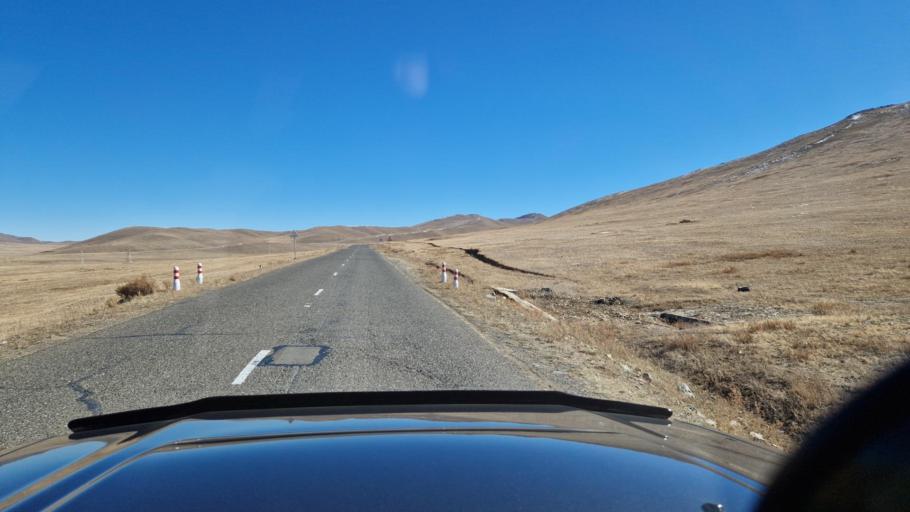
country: MN
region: Hentiy
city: Modot
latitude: 47.8094
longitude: 108.7995
